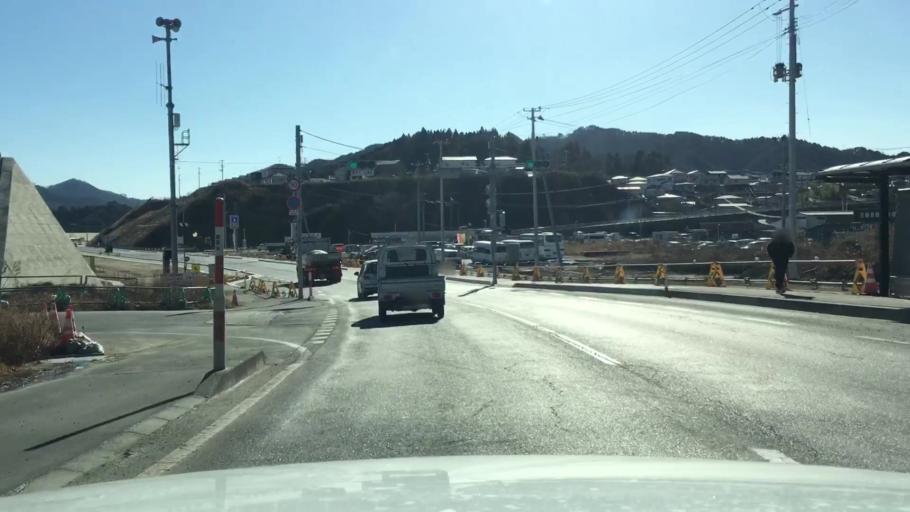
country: JP
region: Iwate
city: Yamada
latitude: 39.4573
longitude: 141.9563
